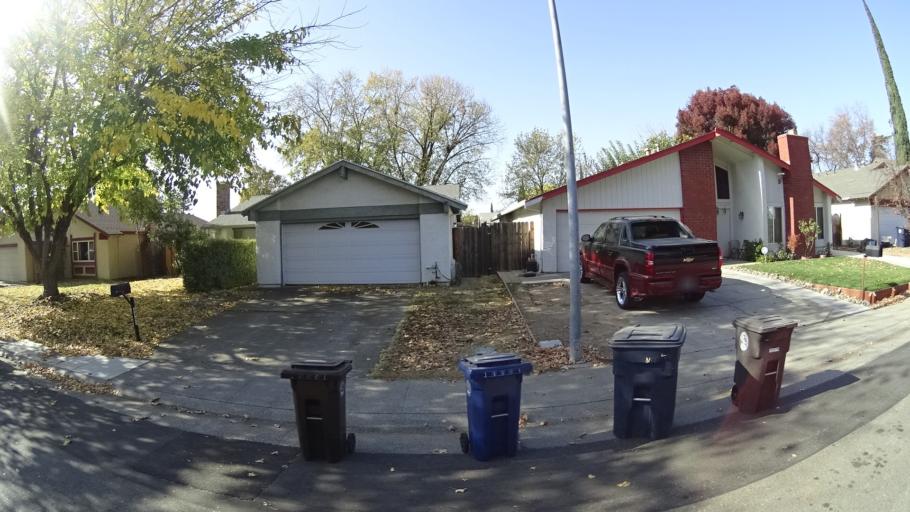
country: US
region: California
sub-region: Sacramento County
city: Citrus Heights
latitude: 38.6907
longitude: -121.2680
